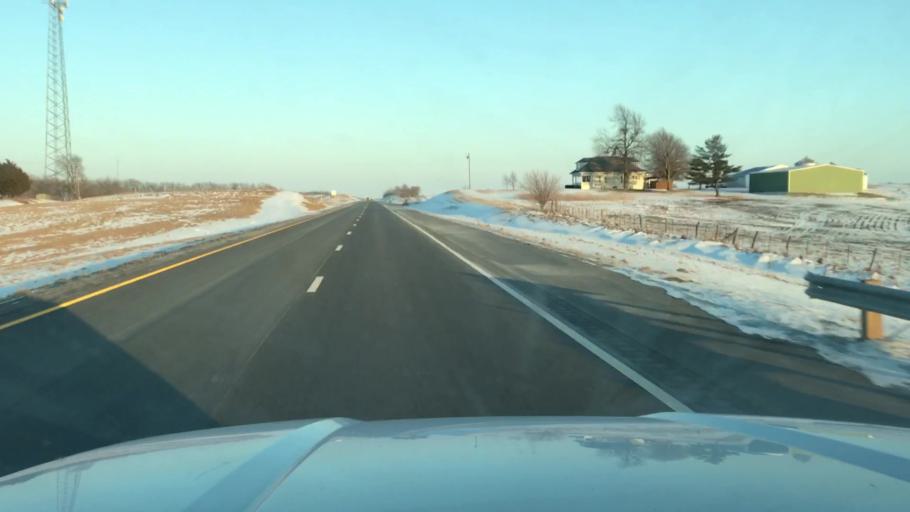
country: US
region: Missouri
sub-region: Clinton County
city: Gower
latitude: 39.7617
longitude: -94.5394
